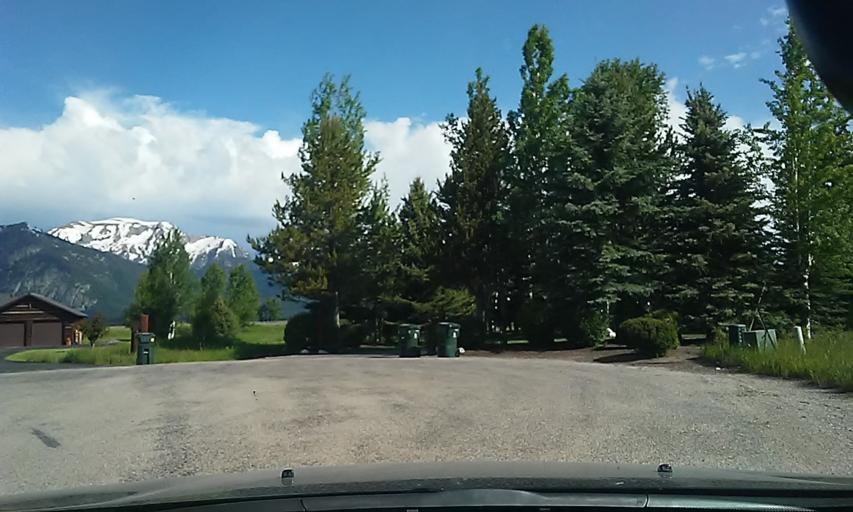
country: US
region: Wyoming
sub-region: Teton County
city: Jackson
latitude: 43.5787
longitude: -110.7571
